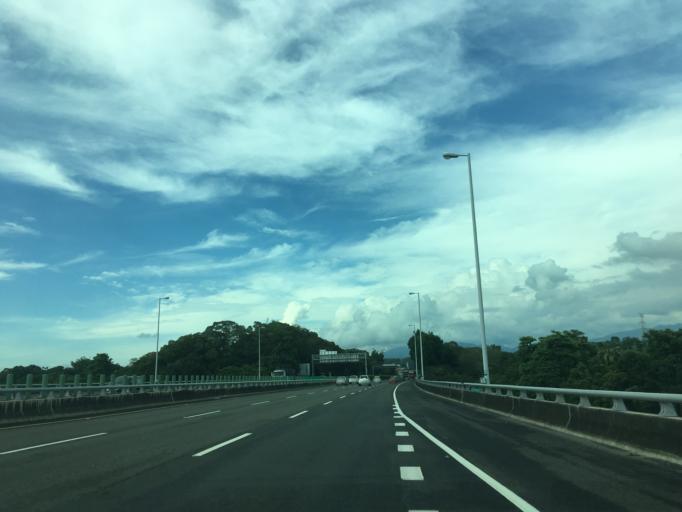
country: TW
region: Taiwan
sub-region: Chiayi
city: Jiayi Shi
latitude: 23.4556
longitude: 120.4885
